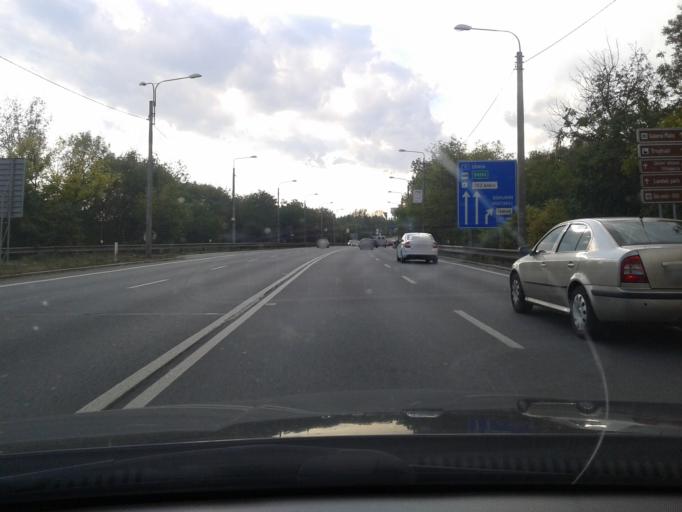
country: CZ
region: Moravskoslezsky
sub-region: Okres Ostrava-Mesto
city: Ostrava
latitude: 49.8038
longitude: 18.2947
